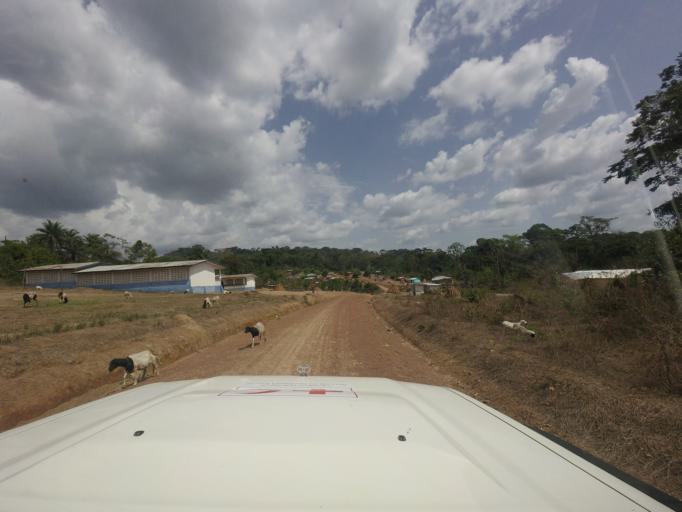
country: LR
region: Lofa
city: Voinjama
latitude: 8.3944
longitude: -9.6409
